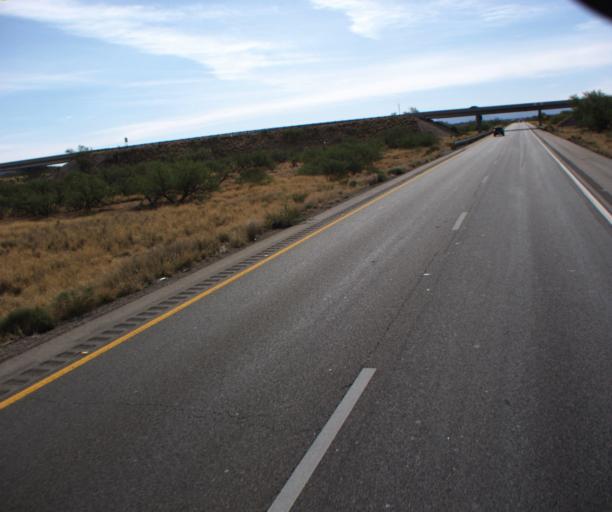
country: US
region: Arizona
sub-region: Pima County
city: Vail
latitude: 32.0281
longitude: -110.7223
